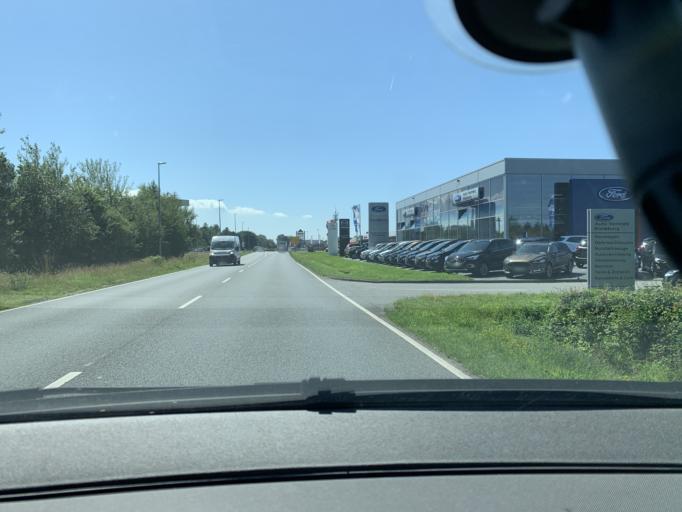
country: DE
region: Schleswig-Holstein
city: Mildstedt
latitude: 54.4911
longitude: 9.0831
